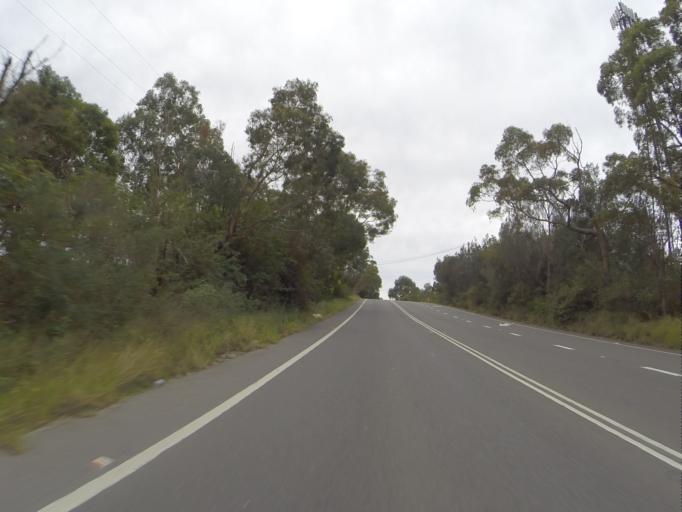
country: AU
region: New South Wales
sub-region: Sutherland Shire
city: Menai
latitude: -34.0361
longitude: 151.0020
